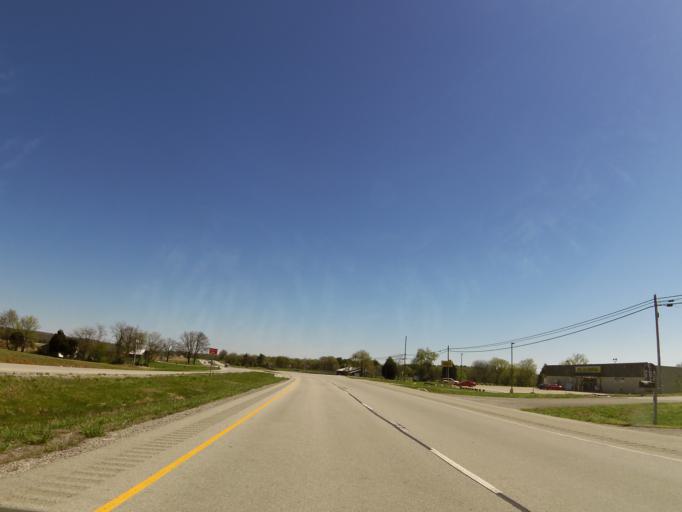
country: US
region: Kentucky
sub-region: Warren County
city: Bowling Green
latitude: 36.9143
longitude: -86.5703
